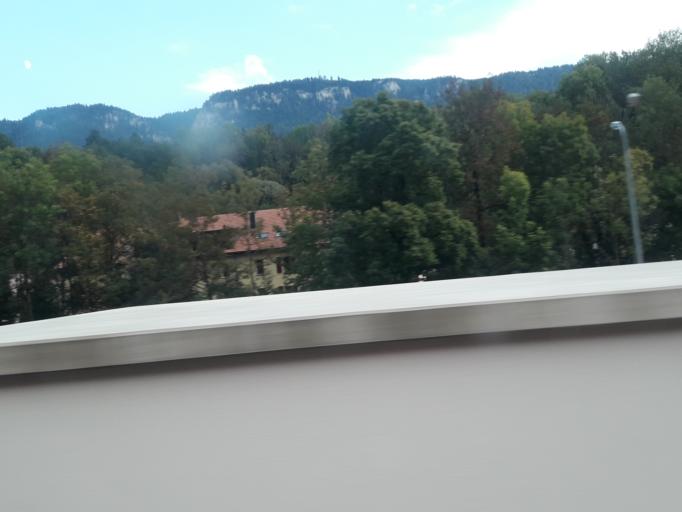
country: CH
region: Bern
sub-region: Jura bernois
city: Moutier
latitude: 47.2815
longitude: 7.3846
